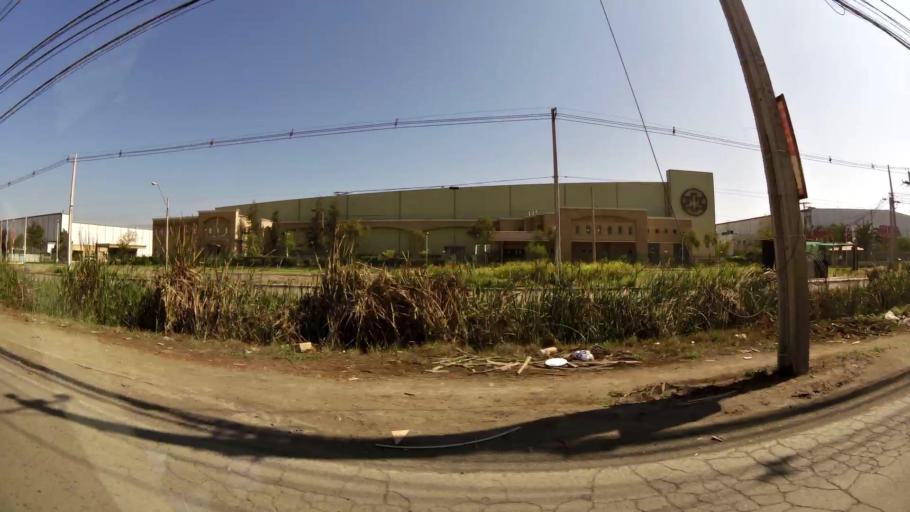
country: CL
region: Santiago Metropolitan
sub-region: Provincia de Chacabuco
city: Chicureo Abajo
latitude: -33.3222
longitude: -70.7386
